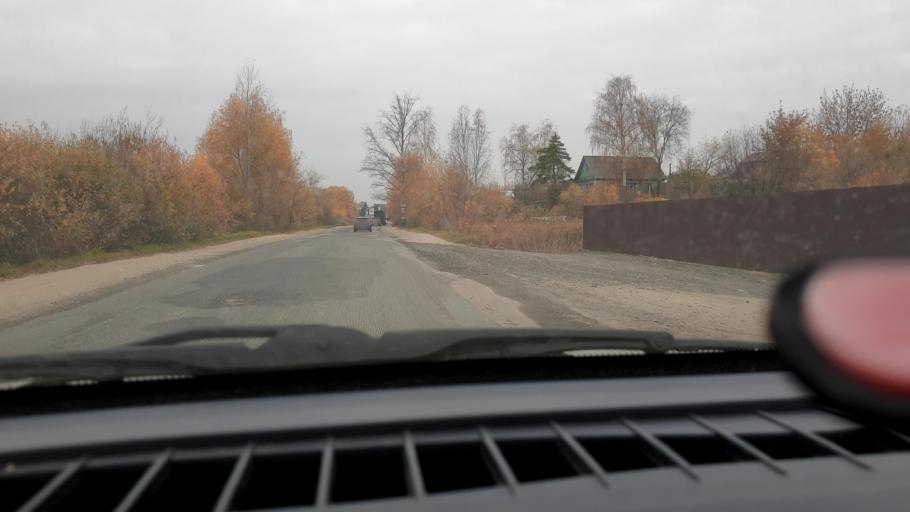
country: RU
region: Nizjnij Novgorod
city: Neklyudovo
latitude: 56.4144
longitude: 43.9727
